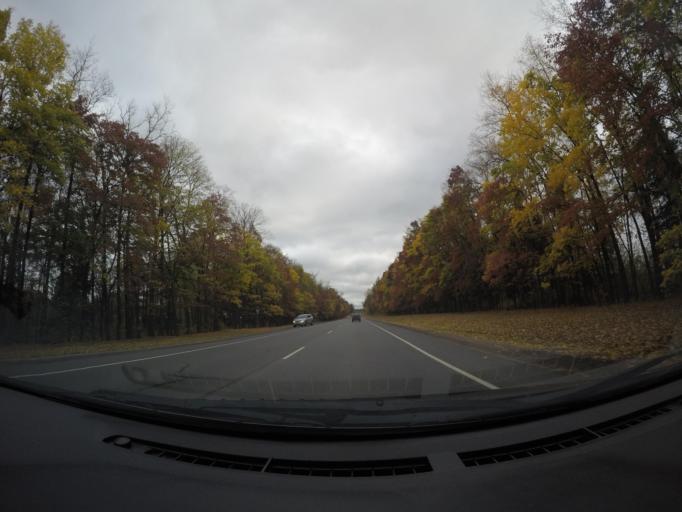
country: RU
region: Moskovskaya
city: Dorokhovo
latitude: 55.5892
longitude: 36.3669
